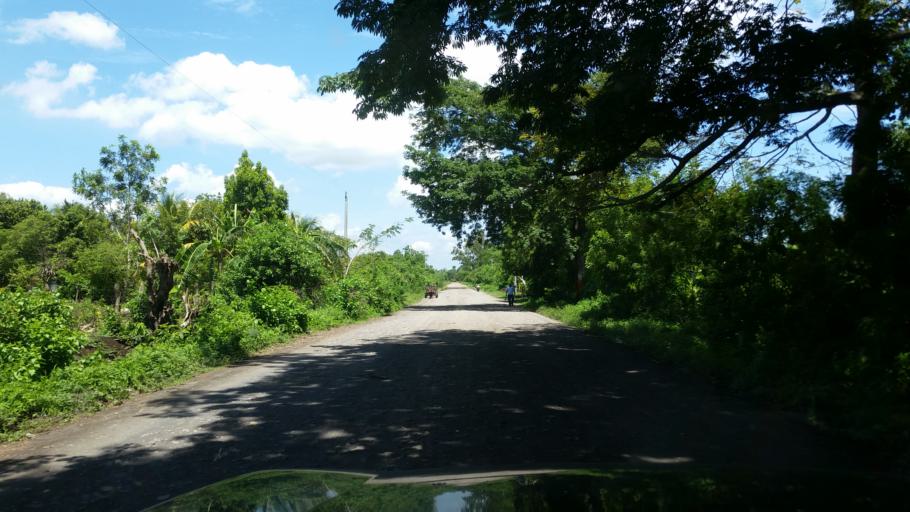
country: NI
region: Chinandega
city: Puerto Morazan
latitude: 12.7730
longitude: -87.1263
